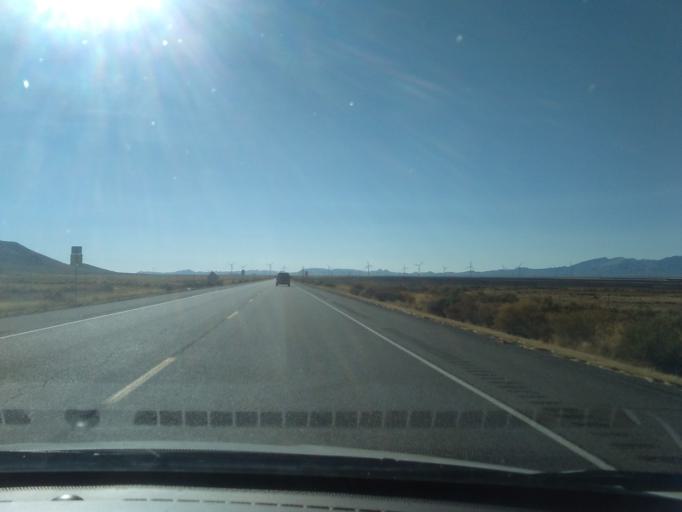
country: US
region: New Mexico
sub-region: Dona Ana County
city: Hatch
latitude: 32.5740
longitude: -107.4532
